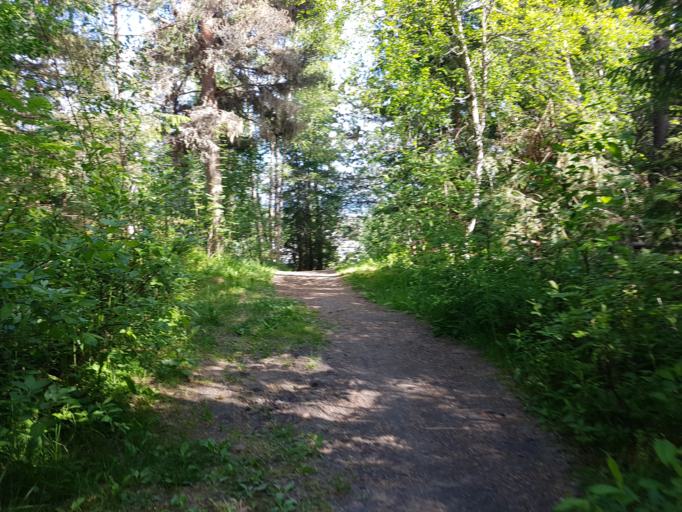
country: NO
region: Sor-Trondelag
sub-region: Trondheim
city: Trondheim
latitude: 63.3989
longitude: 10.3226
